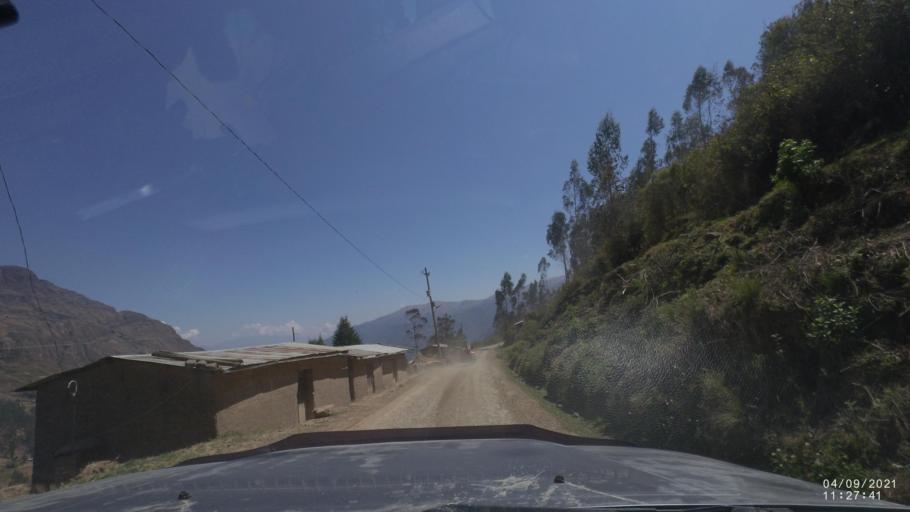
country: BO
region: Cochabamba
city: Colchani
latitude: -17.2489
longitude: -66.5170
